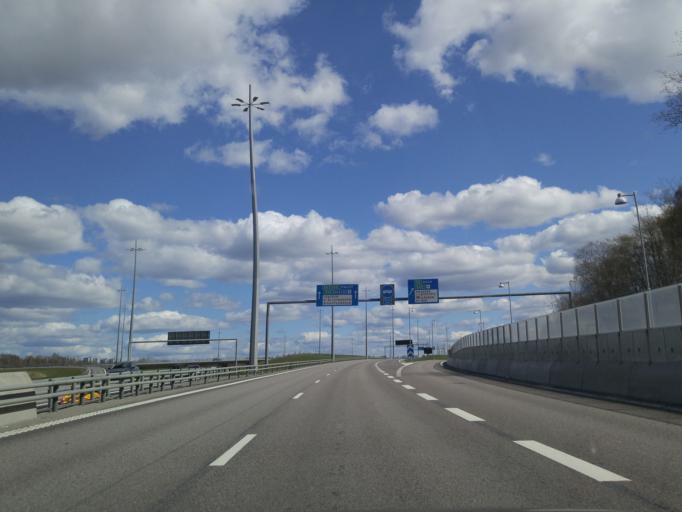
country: SE
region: Vaestra Goetaland
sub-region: Goteborg
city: Majorna
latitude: 57.7043
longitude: 11.8682
